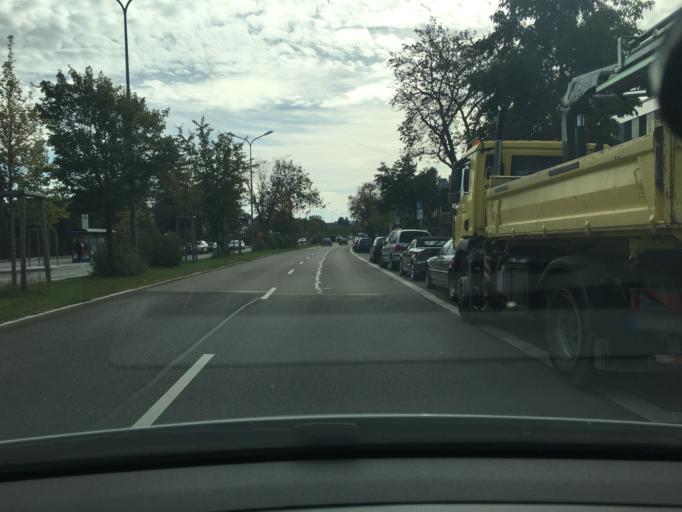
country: DE
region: Bavaria
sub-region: Upper Bavaria
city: Pullach im Isartal
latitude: 48.1095
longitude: 11.5199
